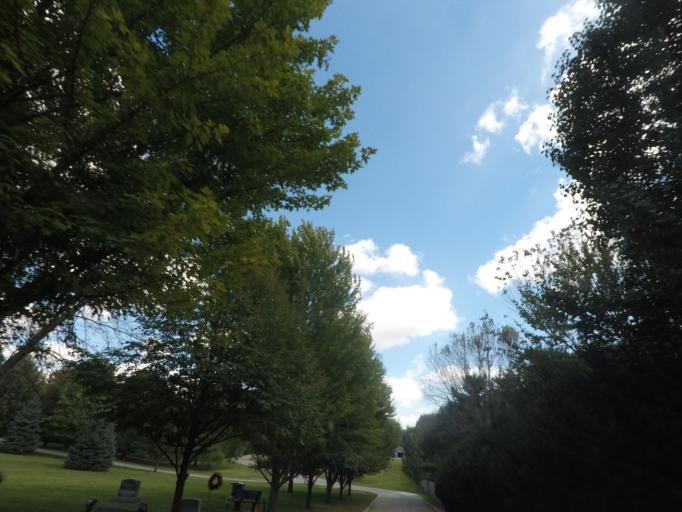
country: US
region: Iowa
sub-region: Story County
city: Nevada
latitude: 42.0212
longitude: -93.4612
